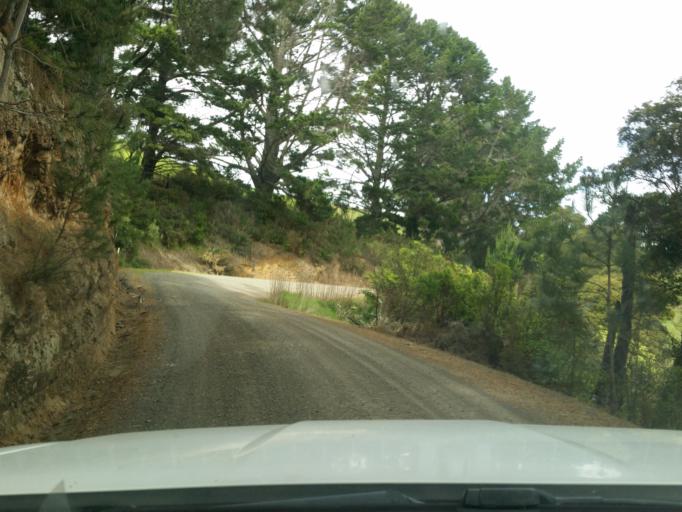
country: NZ
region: Northland
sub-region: Kaipara District
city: Dargaville
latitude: -35.7766
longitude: 173.6657
